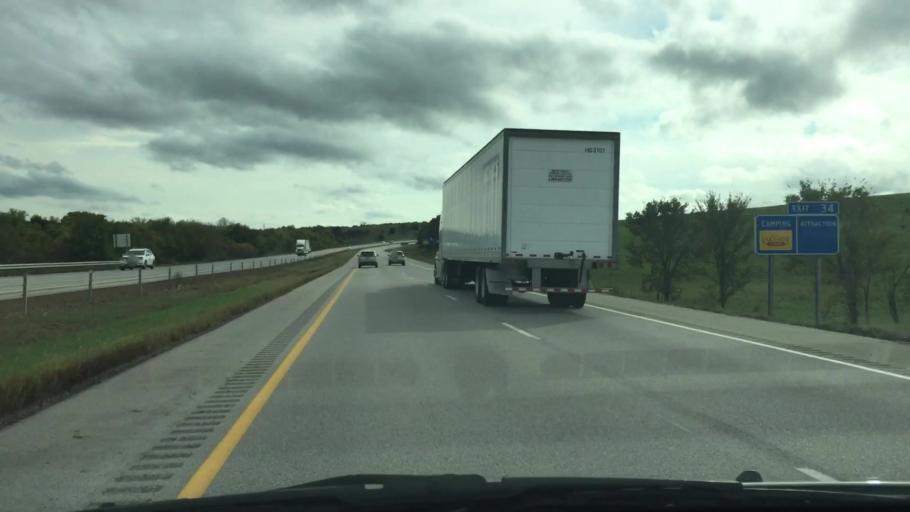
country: US
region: Iowa
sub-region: Clarke County
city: Osceola
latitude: 41.0589
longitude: -93.7818
